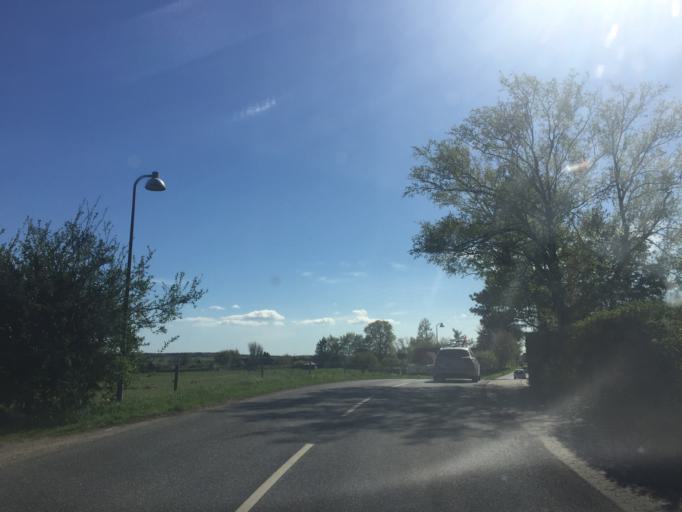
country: DK
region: Capital Region
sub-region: Egedal Kommune
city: Smorumnedre
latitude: 55.7127
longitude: 12.3090
